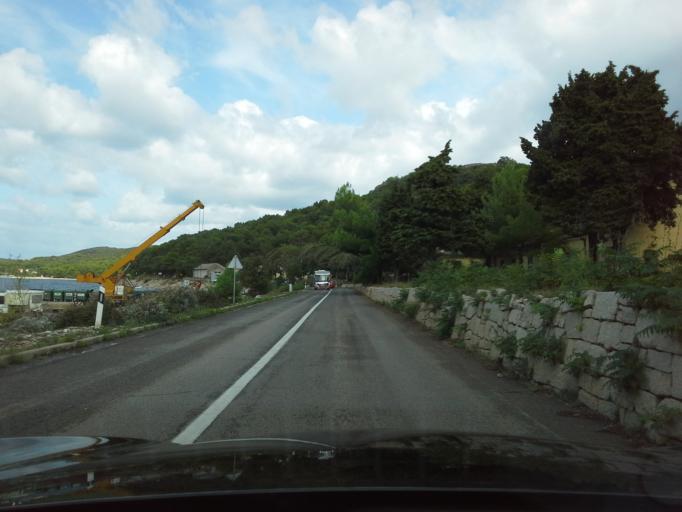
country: HR
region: Primorsko-Goranska
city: Mali Losinj
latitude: 44.5594
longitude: 14.4379
